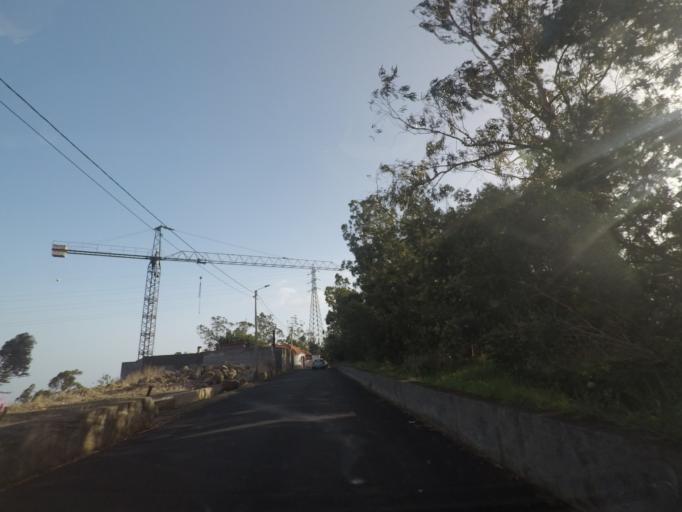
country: PT
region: Madeira
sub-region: Ribeira Brava
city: Campanario
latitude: 32.6682
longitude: -17.0026
